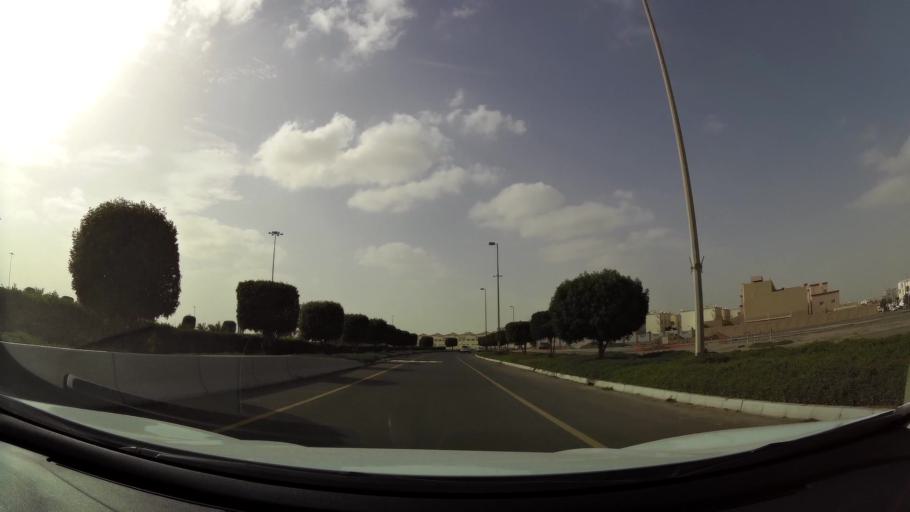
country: AE
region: Abu Dhabi
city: Abu Dhabi
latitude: 24.4003
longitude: 54.5744
